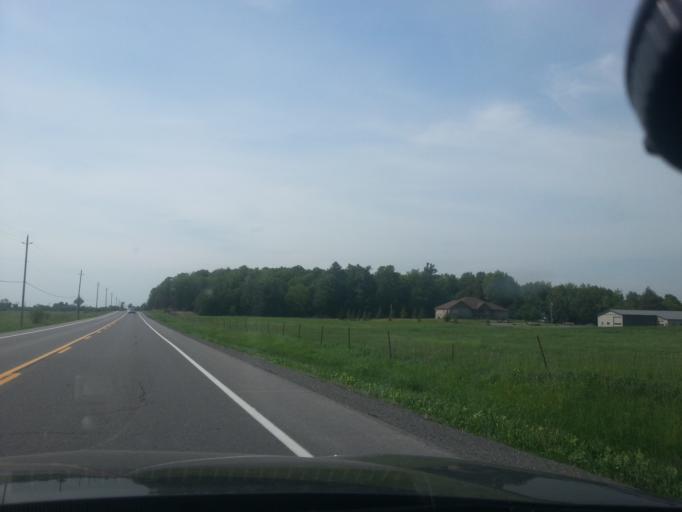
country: CA
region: Ontario
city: Carleton Place
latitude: 45.1669
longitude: -75.9932
